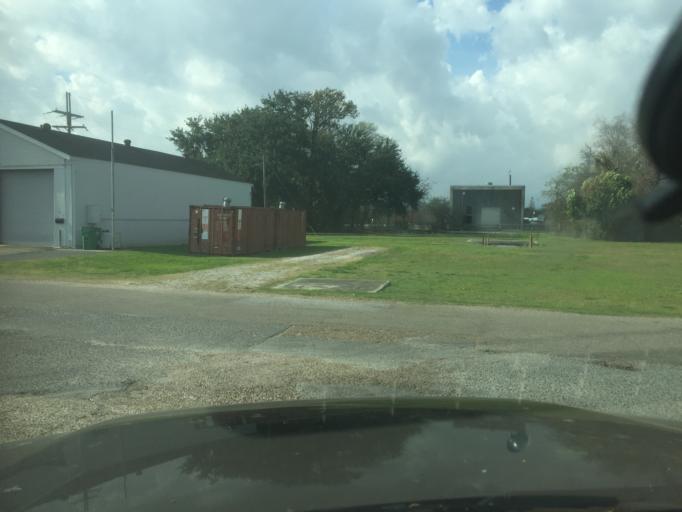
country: US
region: Louisiana
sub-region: Jefferson Parish
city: Avondale
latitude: 29.9108
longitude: -90.2067
